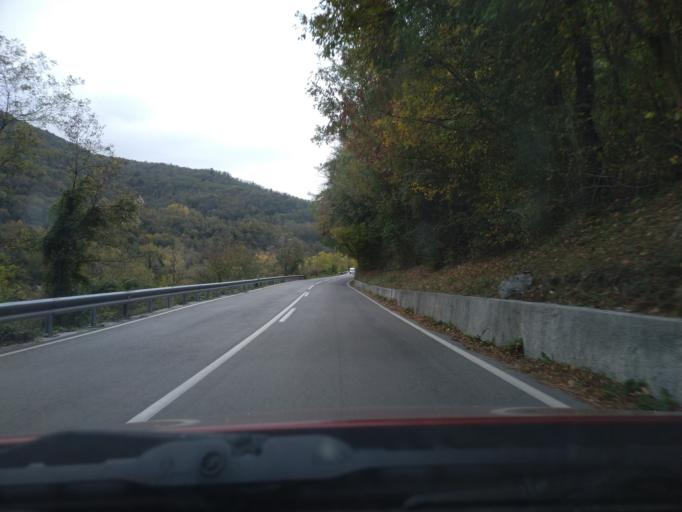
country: SI
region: Kanal
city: Kanal
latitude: 46.1051
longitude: 13.6545
